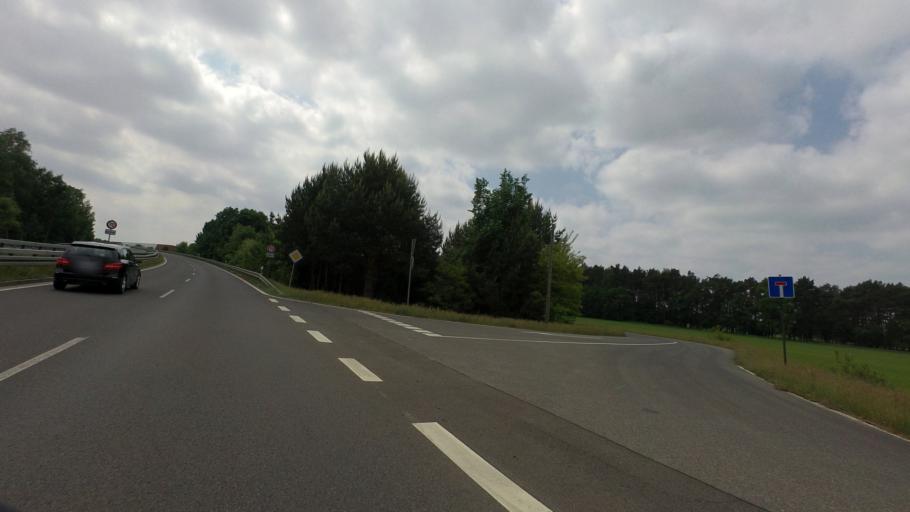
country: DE
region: Brandenburg
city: Peitz
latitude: 51.8196
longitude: 14.3862
